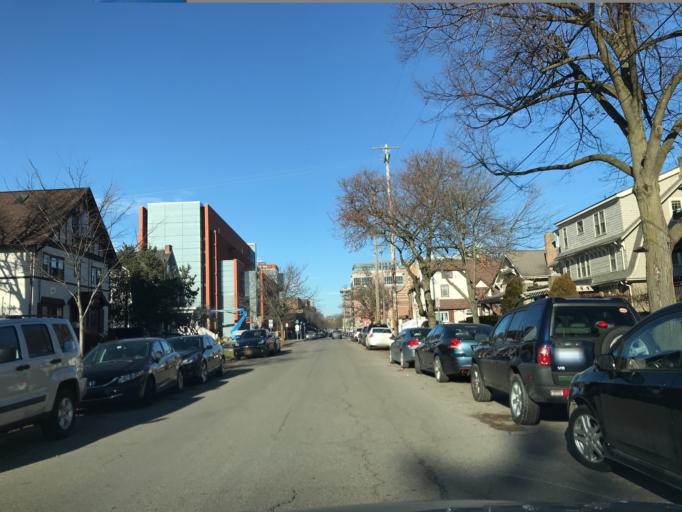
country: US
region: Michigan
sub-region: Washtenaw County
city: Ann Arbor
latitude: 42.2711
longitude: -83.7357
